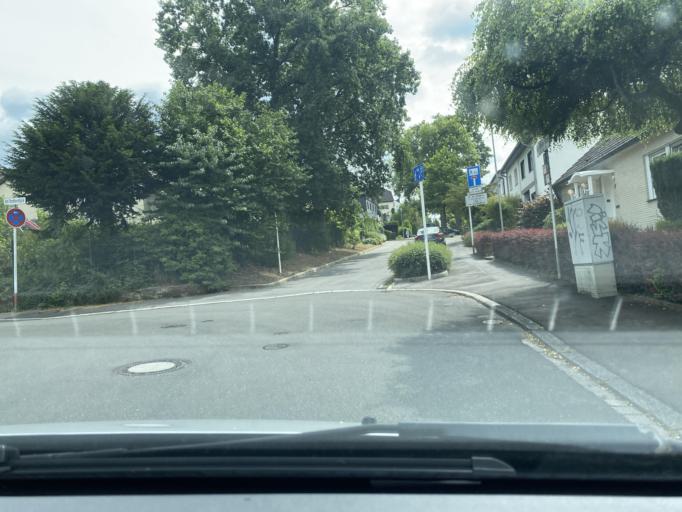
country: DE
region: North Rhine-Westphalia
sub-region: Regierungsbezirk Arnsberg
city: Luedenscheid
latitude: 51.2326
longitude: 7.6146
